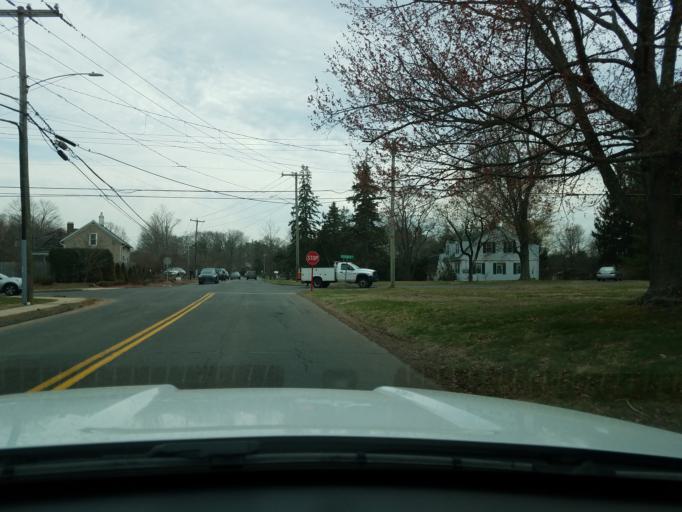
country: US
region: Connecticut
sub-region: Middlesex County
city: Cromwell
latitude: 41.6107
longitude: -72.6669
